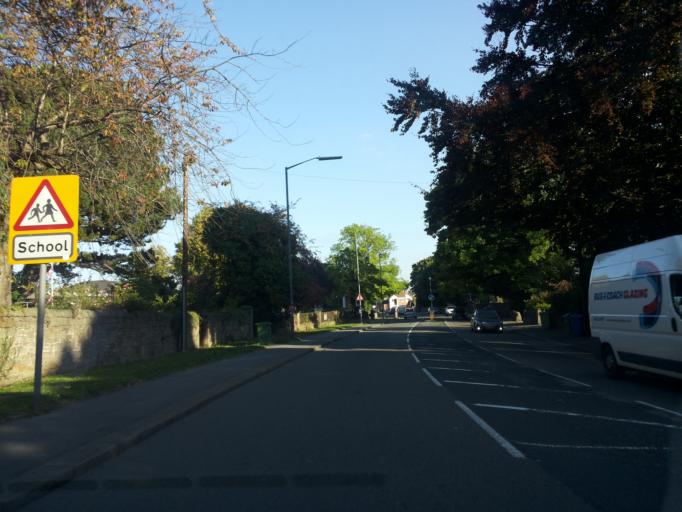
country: GB
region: England
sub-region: Derbyshire
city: Wingerworth
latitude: 53.2315
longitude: -1.4727
